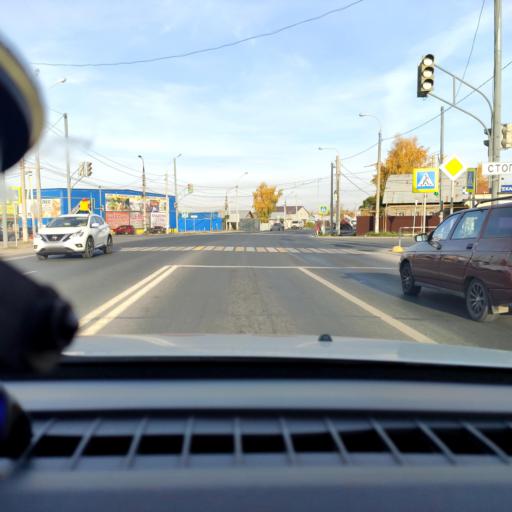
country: RU
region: Samara
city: Volzhskiy
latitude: 53.4261
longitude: 50.1219
